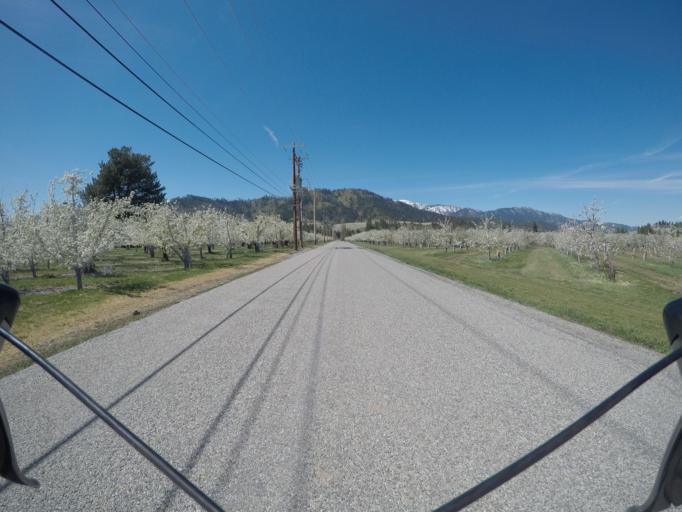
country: US
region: Washington
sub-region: Chelan County
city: Leavenworth
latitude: 47.5642
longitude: -120.5937
